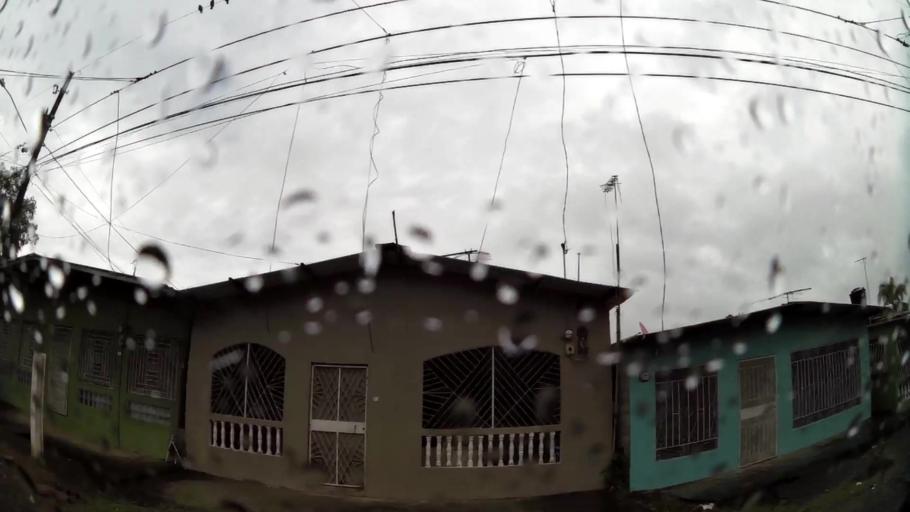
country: PA
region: Colon
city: Las Margaritas
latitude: 9.3327
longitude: -79.8680
